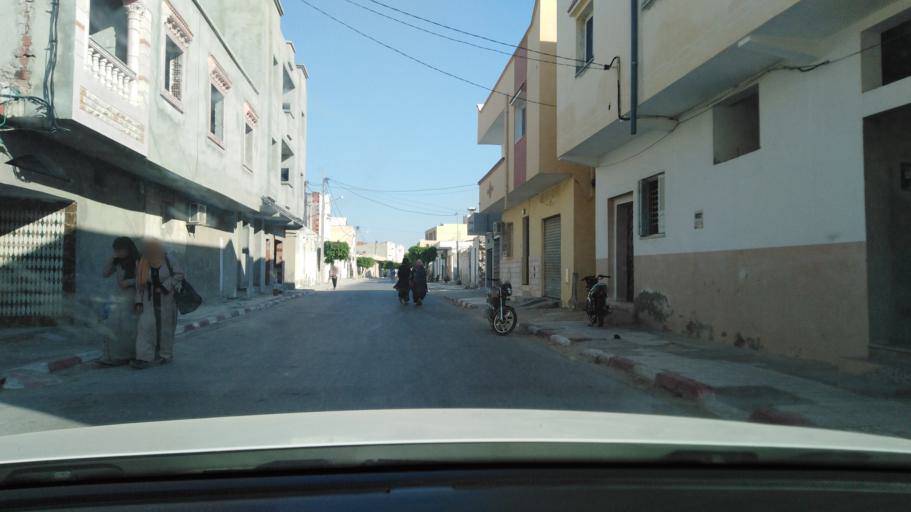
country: TN
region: Qabis
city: Gabes
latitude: 33.9376
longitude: 10.0682
